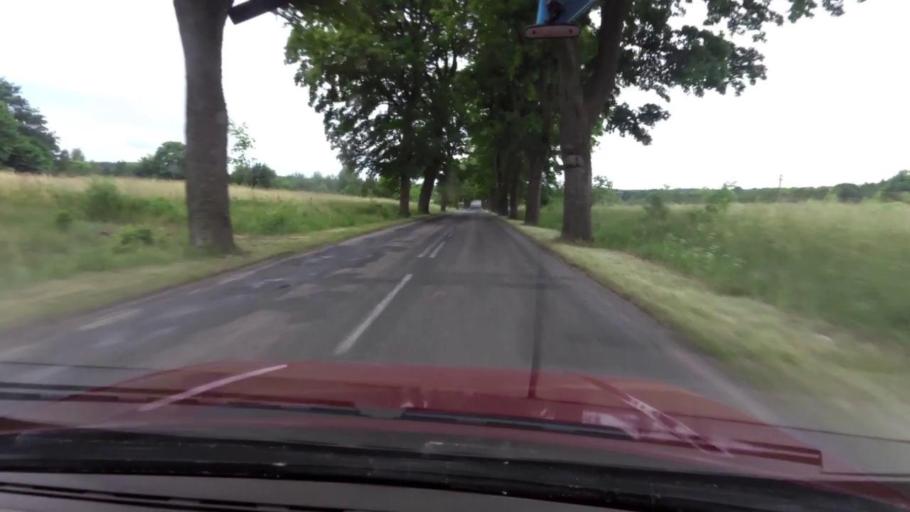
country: PL
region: West Pomeranian Voivodeship
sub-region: Powiat koszalinski
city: Sianow
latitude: 54.1753
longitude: 16.3907
